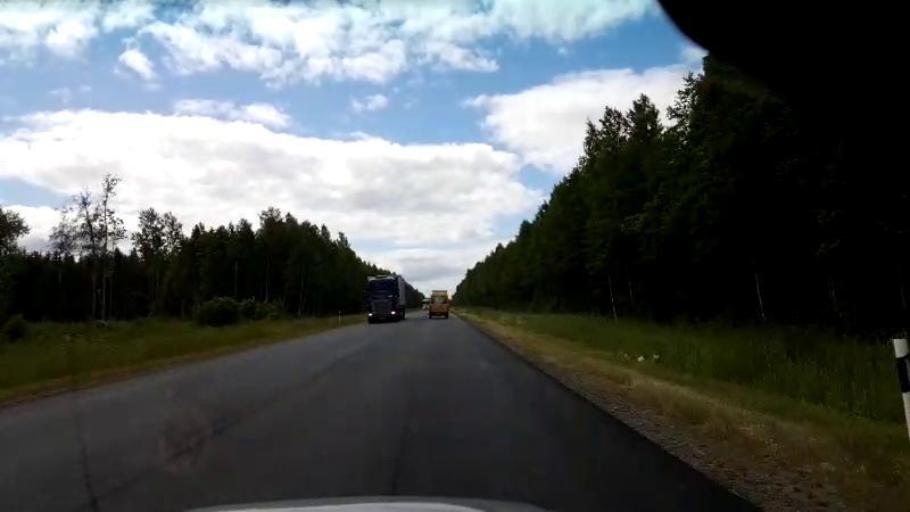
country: LV
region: Salacgrivas
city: Ainazi
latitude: 57.9204
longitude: 24.4226
